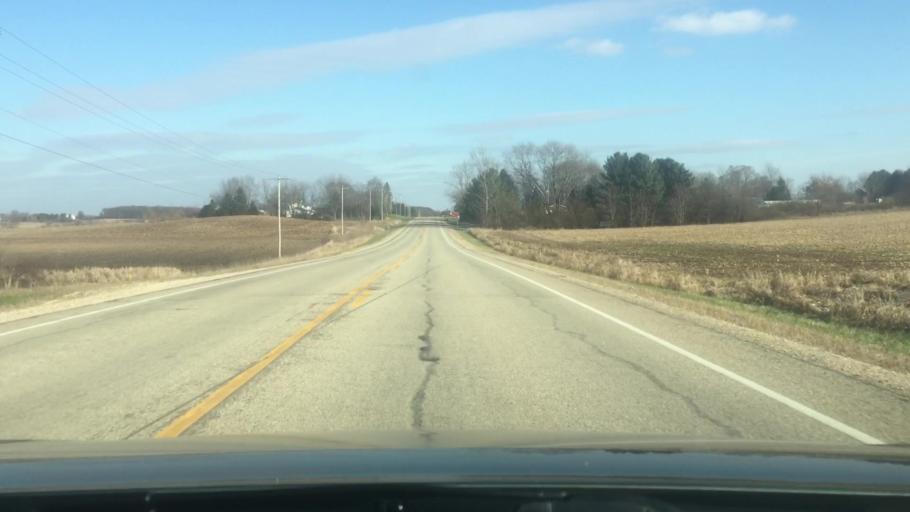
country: US
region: Wisconsin
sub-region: Jefferson County
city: Fort Atkinson
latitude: 42.9389
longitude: -88.7586
